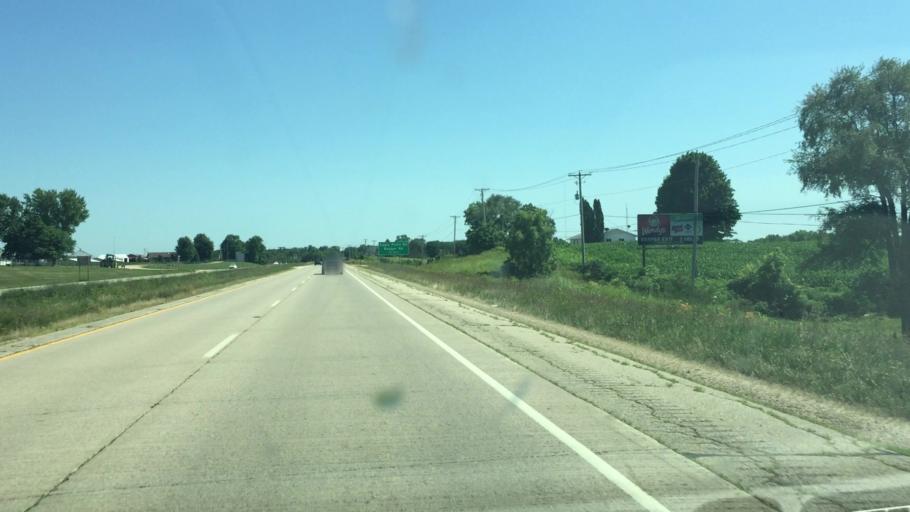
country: US
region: Wisconsin
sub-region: Grant County
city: Dickeyville
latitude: 42.5646
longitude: -90.6115
